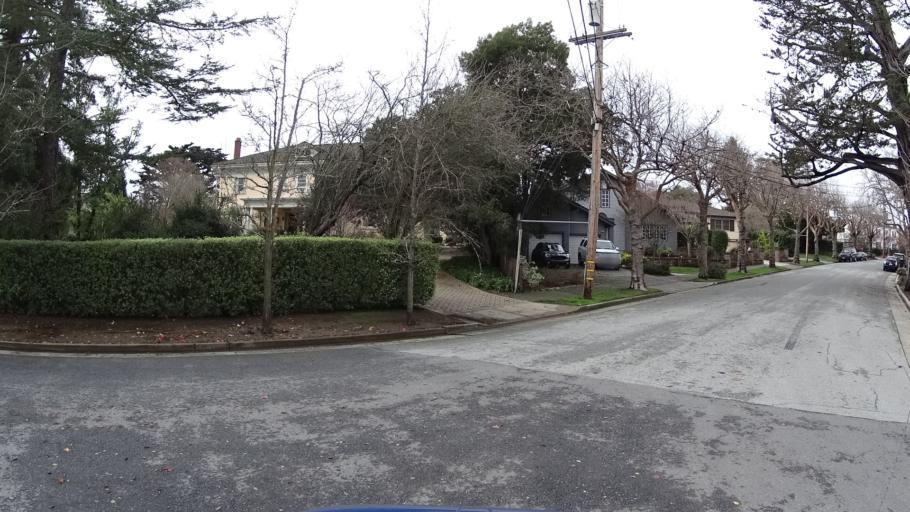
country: US
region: California
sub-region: San Mateo County
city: San Mateo
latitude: 37.5713
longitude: -122.3458
